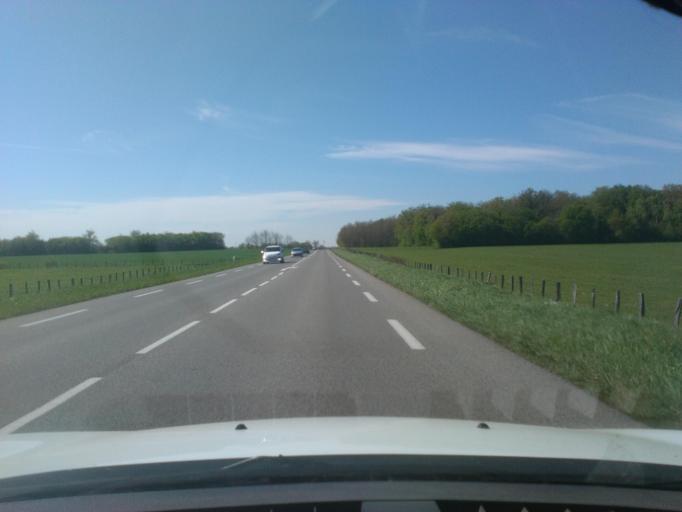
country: FR
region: Rhone-Alpes
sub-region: Departement de l'Ain
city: Villars-les-Dombes
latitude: 46.0347
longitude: 5.0646
